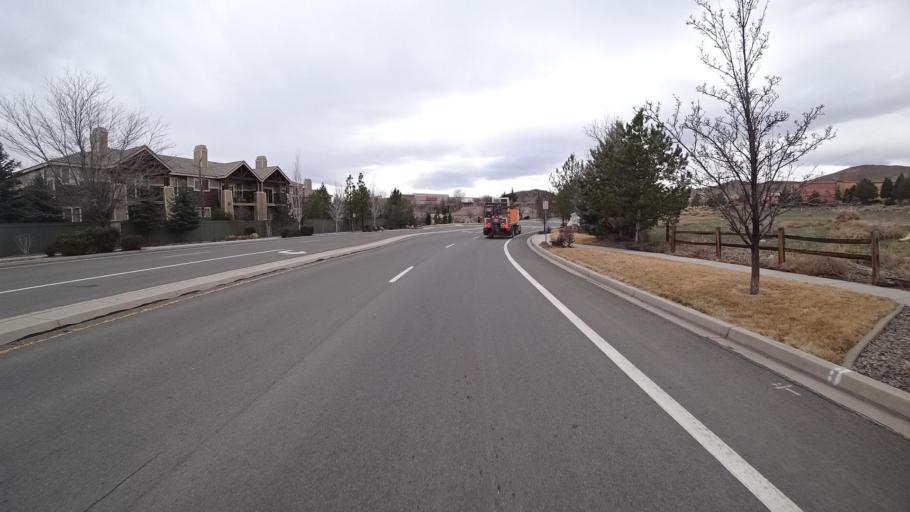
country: US
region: Nevada
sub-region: Washoe County
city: Sun Valley
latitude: 39.5819
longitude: -119.7373
